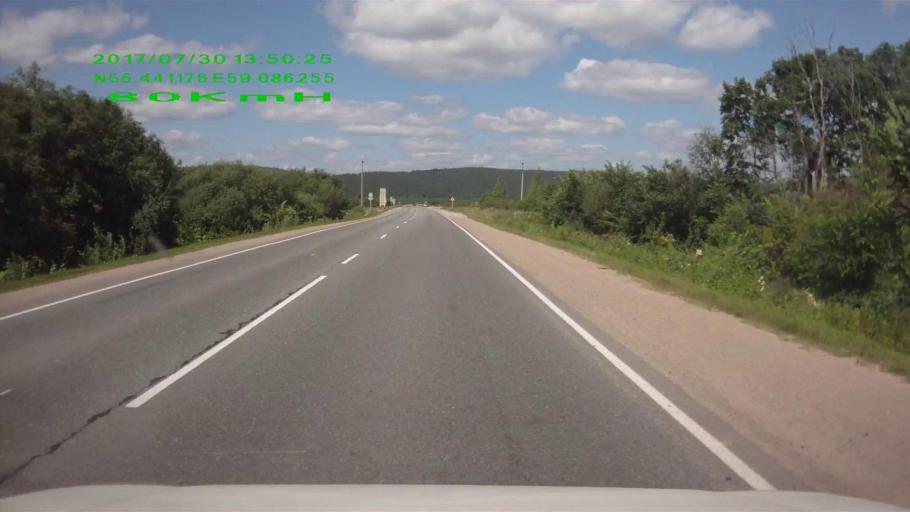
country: RU
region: Sverdlovsk
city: Mikhaylovsk
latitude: 56.4417
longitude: 59.0861
